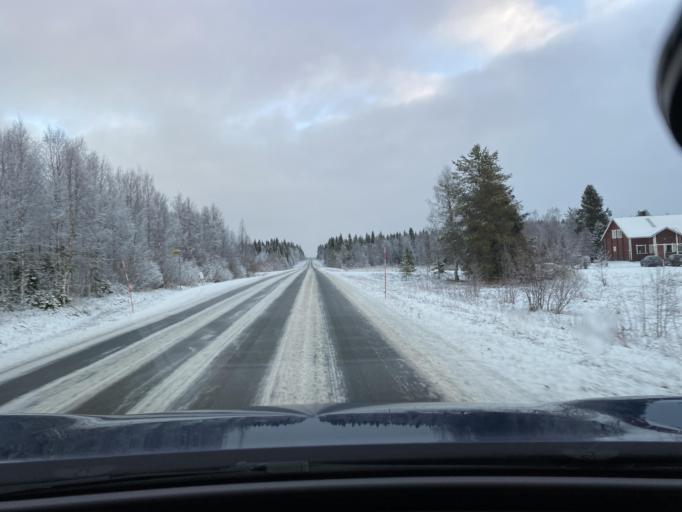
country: FI
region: Lapland
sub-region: Rovaniemi
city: Ranua
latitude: 65.9714
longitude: 26.1024
